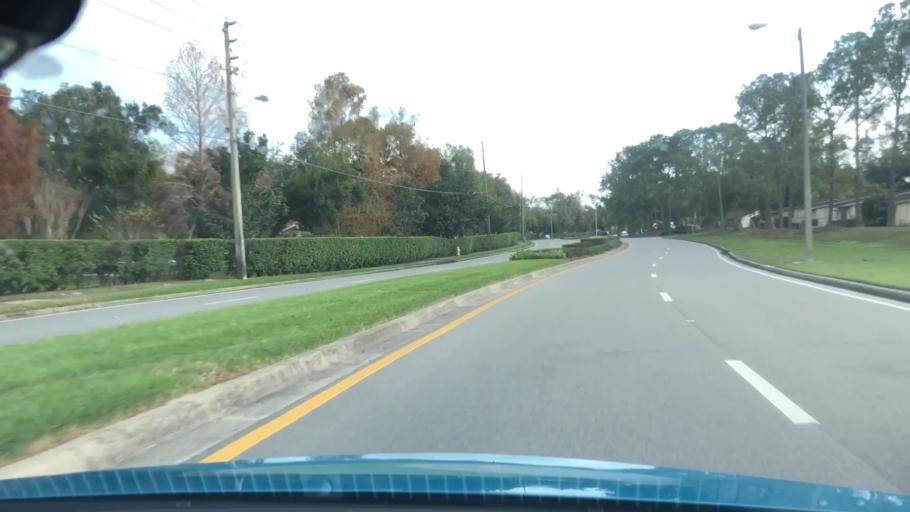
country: US
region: Florida
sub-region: Seminole County
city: Heathrow
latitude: 28.7514
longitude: -81.3463
